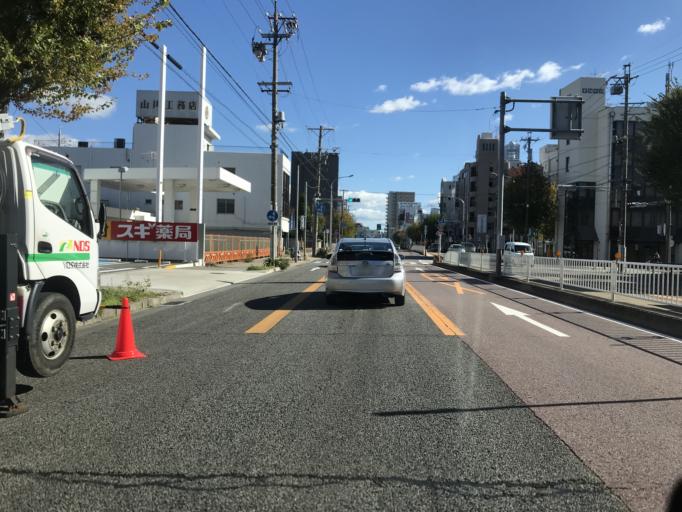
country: JP
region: Aichi
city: Nagoya-shi
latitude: 35.1820
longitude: 136.9362
